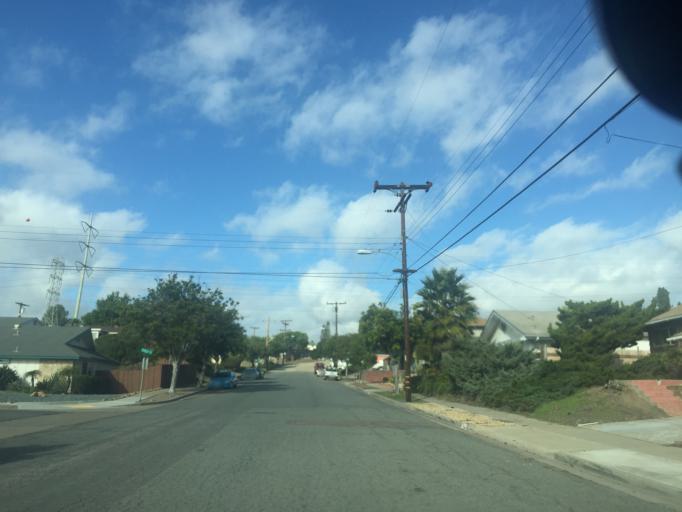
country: US
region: California
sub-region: San Diego County
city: San Diego
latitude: 32.7825
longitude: -117.1507
